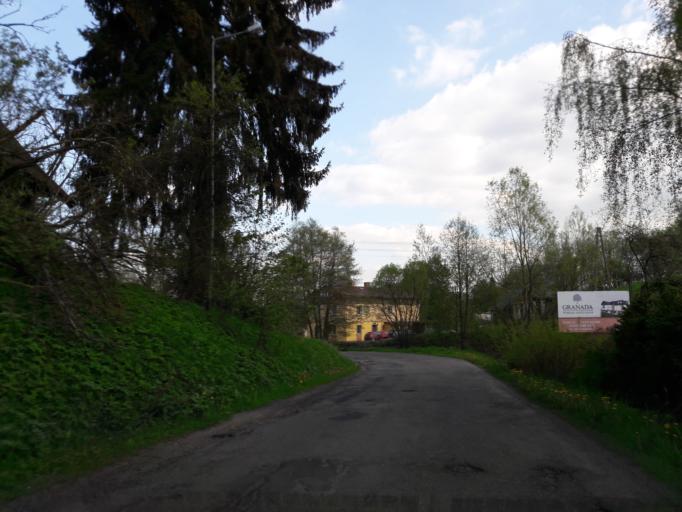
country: PL
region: Lower Silesian Voivodeship
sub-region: Powiat klodzki
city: Duszniki-Zdroj
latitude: 50.4375
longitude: 16.3574
